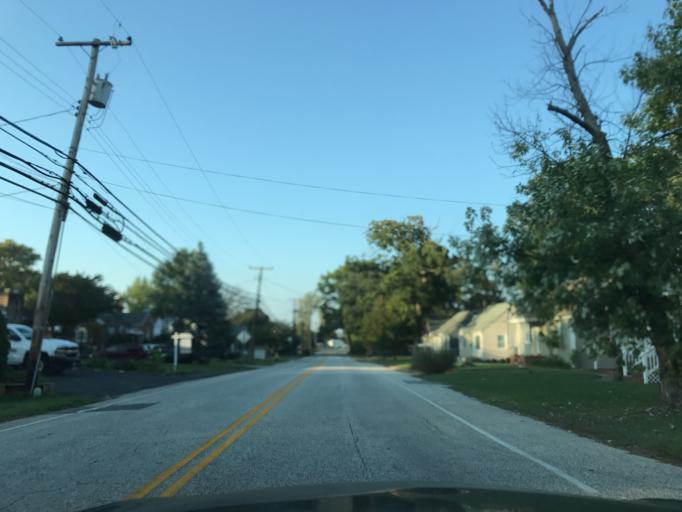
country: US
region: Maryland
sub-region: Anne Arundel County
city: Glen Burnie
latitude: 39.1546
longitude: -76.6224
